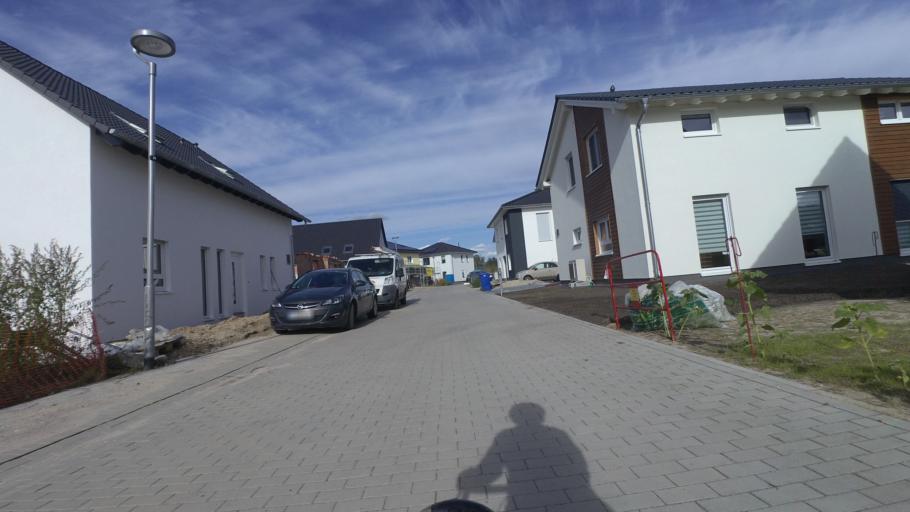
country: DE
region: Brandenburg
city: Ludwigsfelde
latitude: 52.3144
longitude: 13.2214
